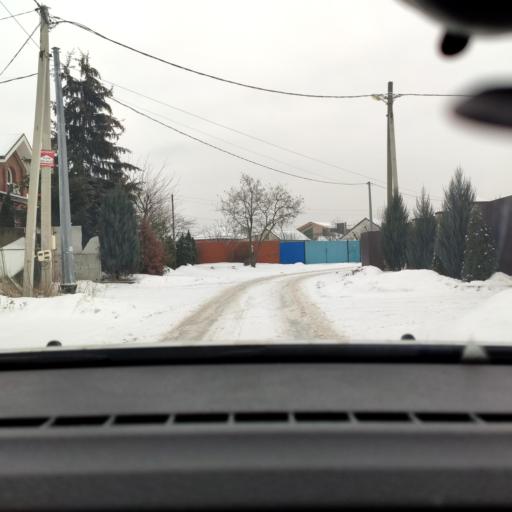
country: RU
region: Voronezj
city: Podgornoye
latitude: 51.7959
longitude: 39.1403
